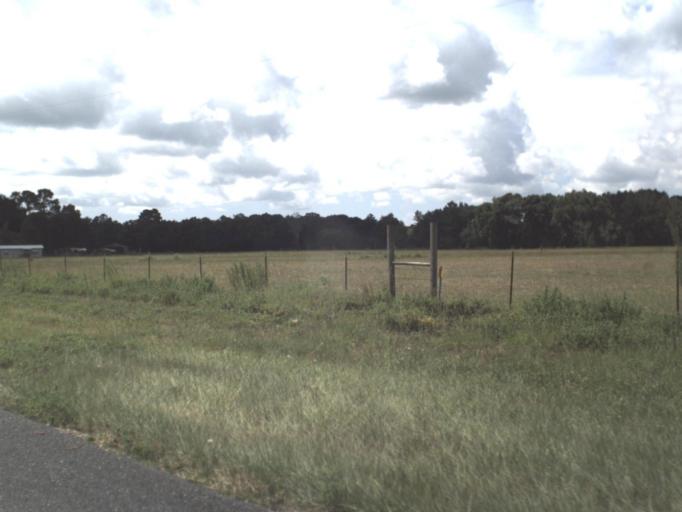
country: US
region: Florida
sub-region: Taylor County
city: Perry
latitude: 30.1717
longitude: -83.6313
